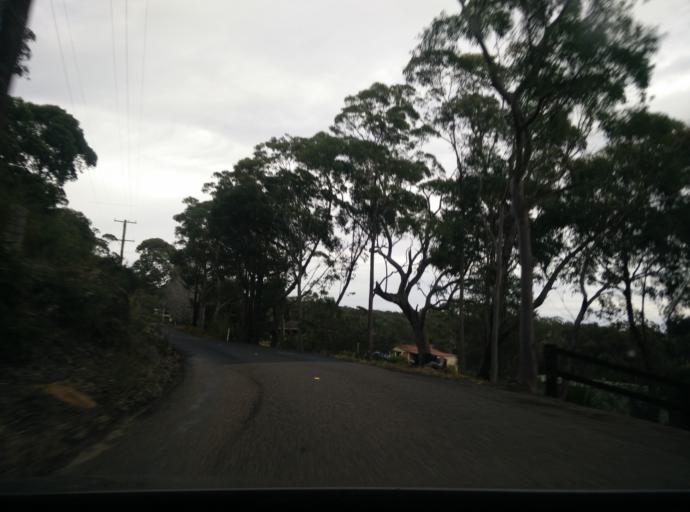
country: AU
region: New South Wales
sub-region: Gosford Shire
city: Narara
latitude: -33.3628
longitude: 151.3066
